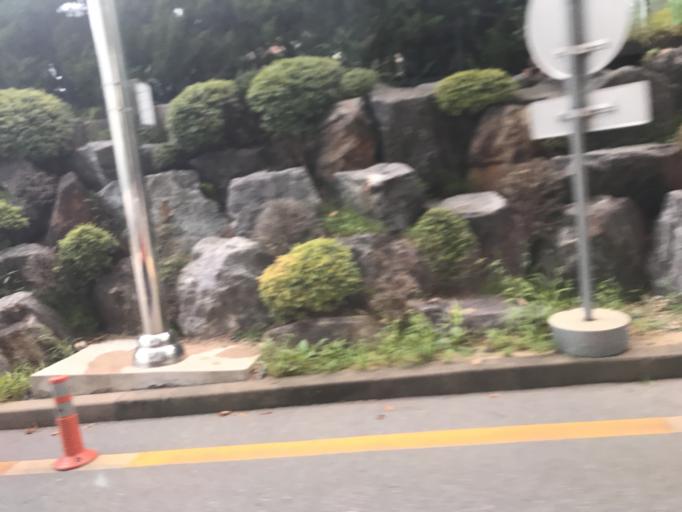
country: KR
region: Seoul
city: Seoul
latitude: 37.5645
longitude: 126.9419
